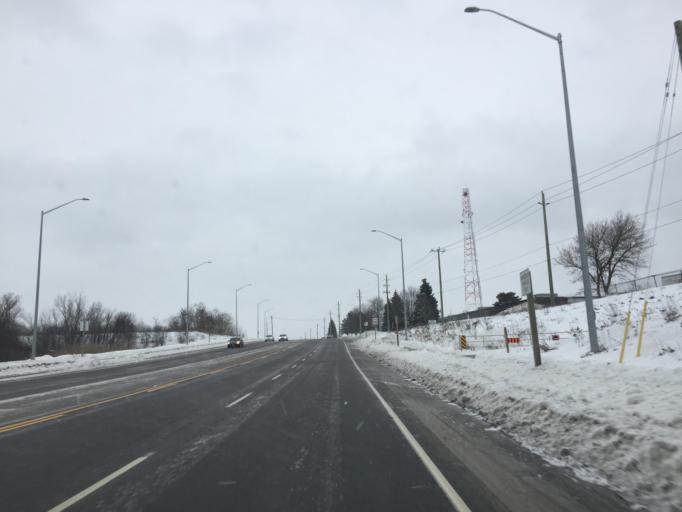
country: CA
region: Ontario
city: Waterloo
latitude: 43.4676
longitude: -80.4643
